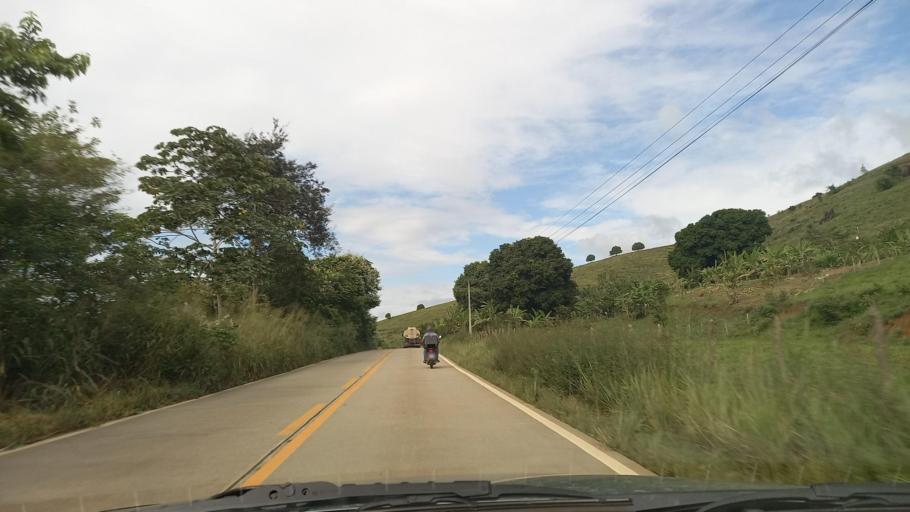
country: BR
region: Pernambuco
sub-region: Maraial
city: Maraial
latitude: -8.7503
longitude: -35.8239
